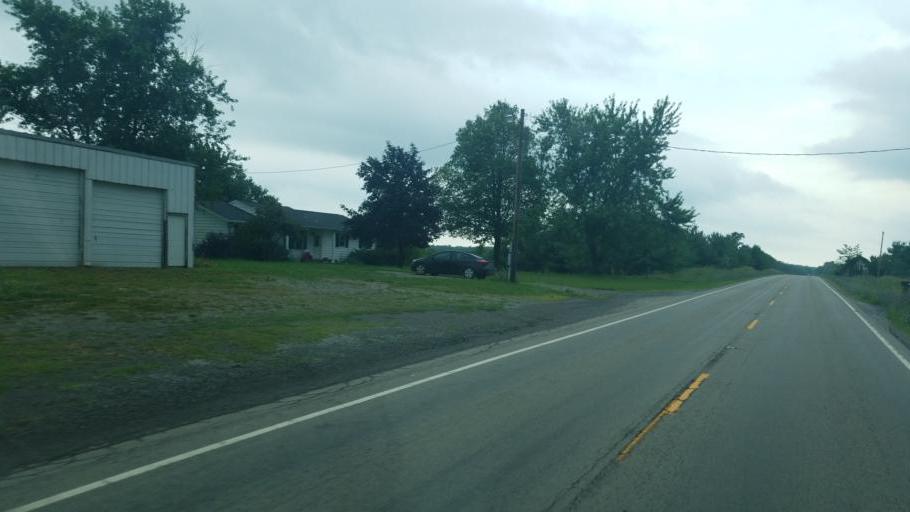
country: US
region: Ohio
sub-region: Logan County
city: Russells Point
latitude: 40.5756
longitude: -83.8388
